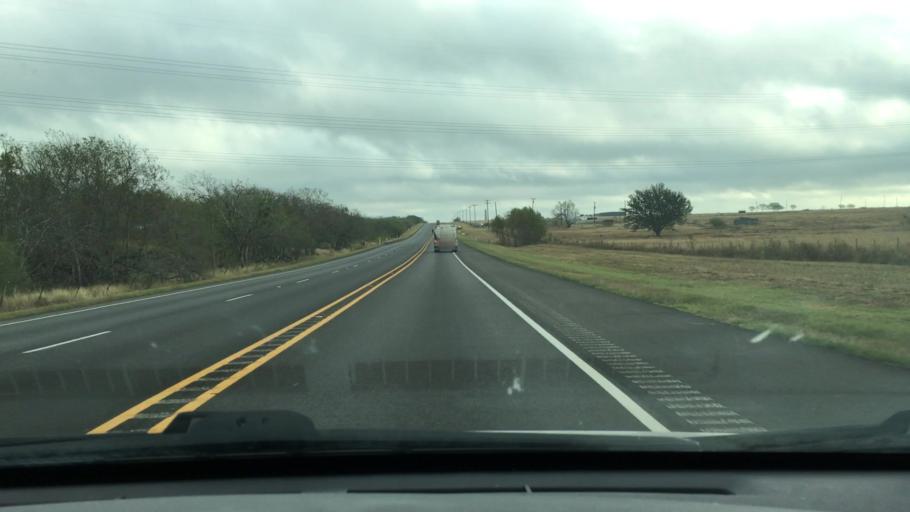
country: US
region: Texas
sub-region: Gonzales County
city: Nixon
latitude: 29.2578
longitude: -97.8065
